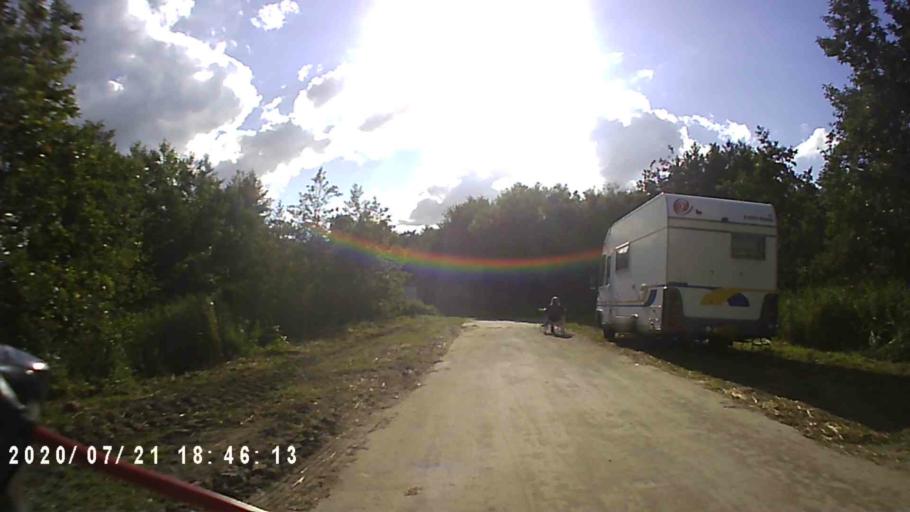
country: NL
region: Groningen
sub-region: Gemeente Hoogezand-Sappemeer
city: Hoogezand
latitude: 53.2097
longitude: 6.7490
